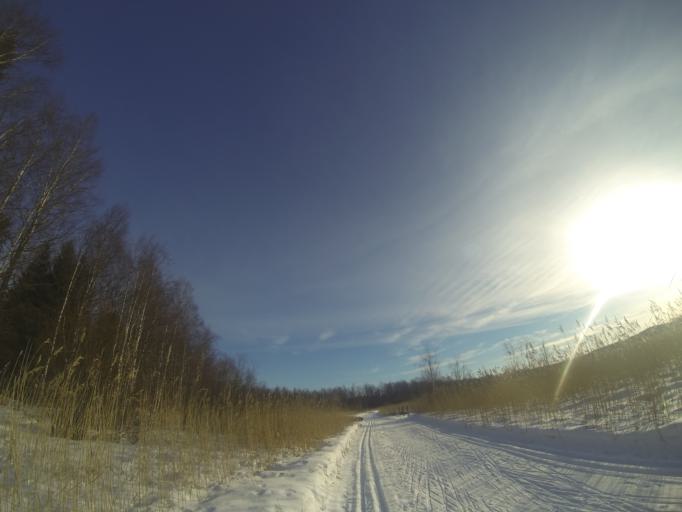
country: FI
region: Southern Savonia
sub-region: Savonlinna
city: Savonlinna
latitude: 61.9119
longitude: 28.9185
